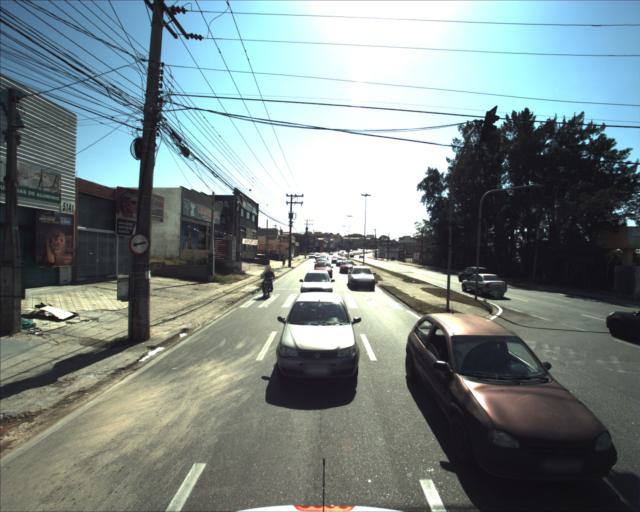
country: BR
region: Sao Paulo
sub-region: Sorocaba
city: Sorocaba
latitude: -23.4429
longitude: -47.4786
